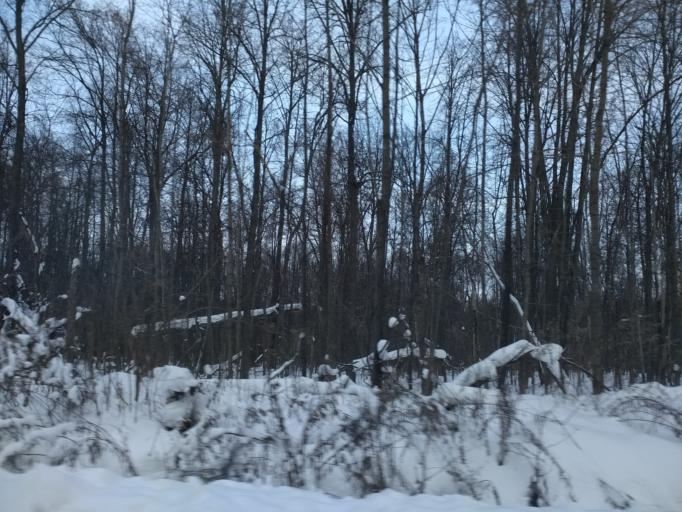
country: RU
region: Bashkortostan
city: Kudeyevskiy
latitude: 54.7143
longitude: 56.6360
